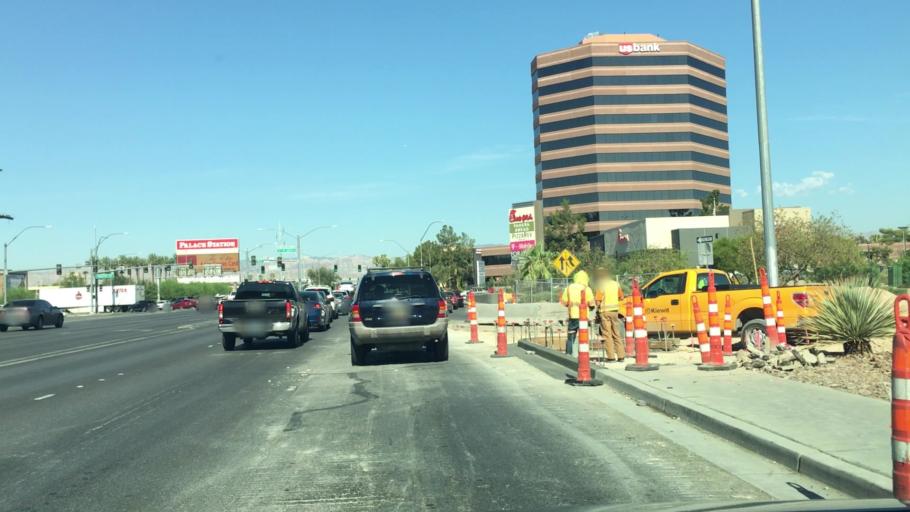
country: US
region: Nevada
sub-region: Clark County
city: Las Vegas
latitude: 36.1444
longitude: -115.1715
